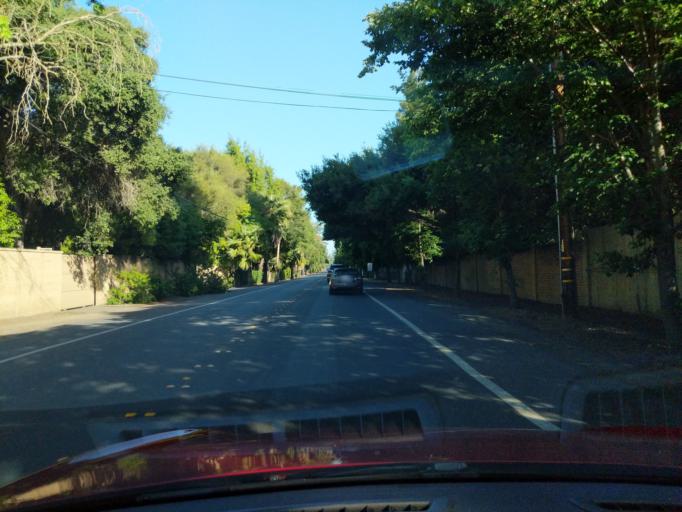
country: US
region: California
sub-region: San Mateo County
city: Menlo Park
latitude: 37.4626
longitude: -122.1799
